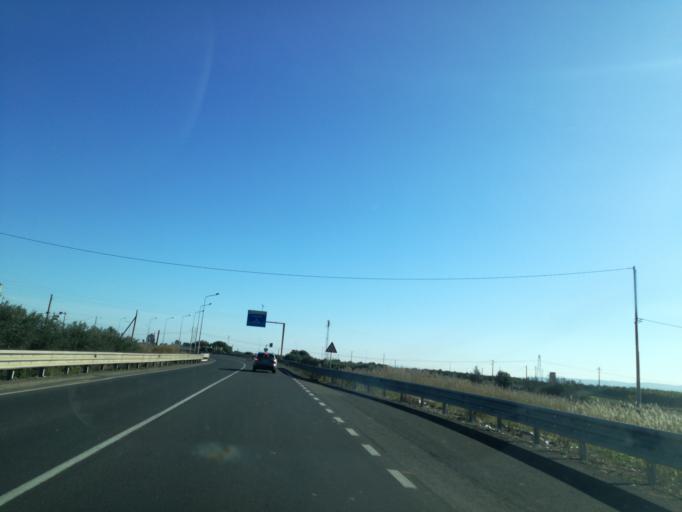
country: IT
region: Sicily
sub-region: Catania
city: Scordia
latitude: 37.3797
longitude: 14.8200
